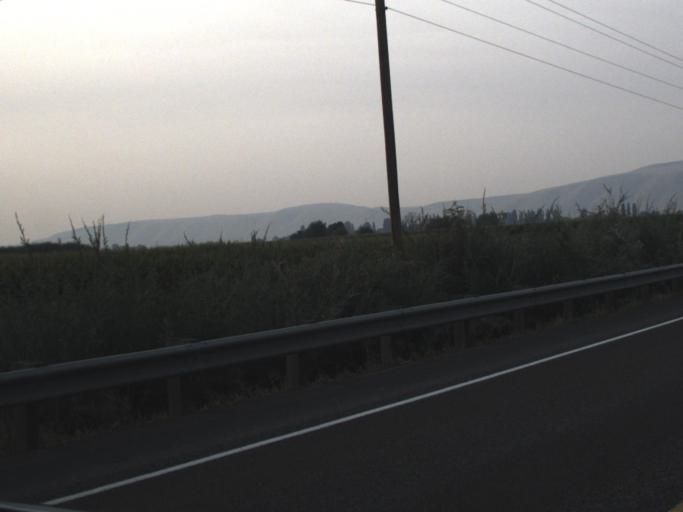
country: US
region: Washington
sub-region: Yakima County
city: Toppenish
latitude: 46.3511
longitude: -120.3205
